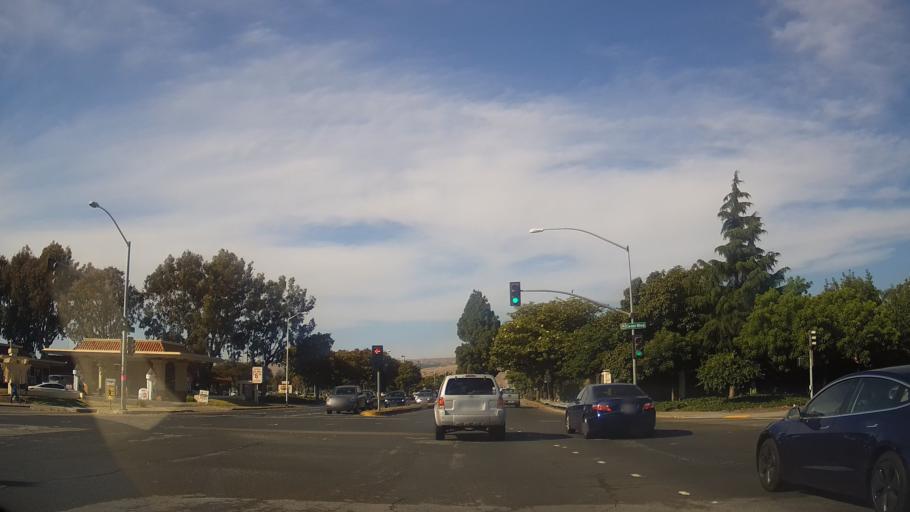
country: US
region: California
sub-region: Alameda County
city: Newark
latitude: 37.5420
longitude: -122.0264
